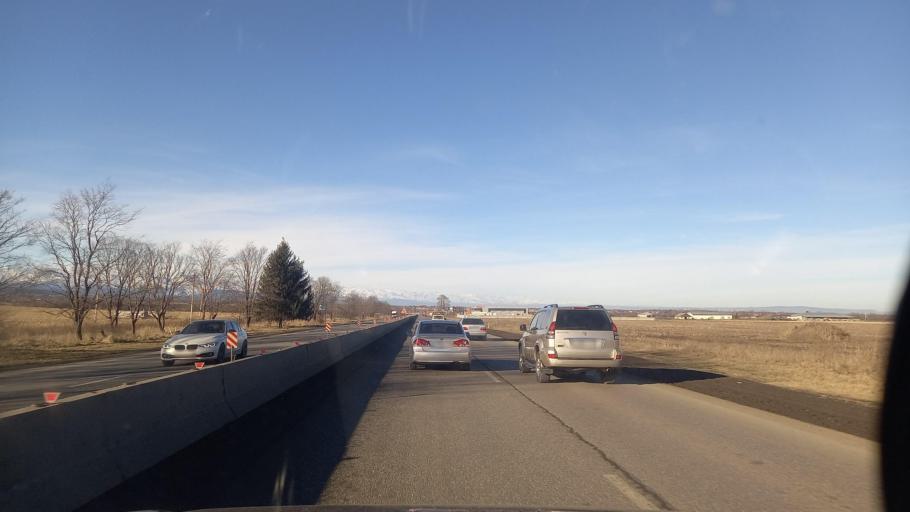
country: RU
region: North Ossetia
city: Vladikavkaz
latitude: 43.0258
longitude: 44.6230
